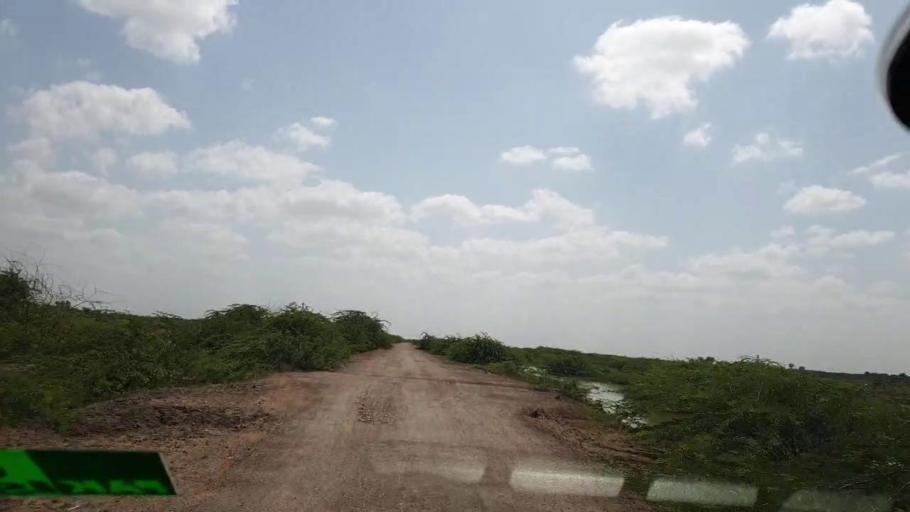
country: PK
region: Sindh
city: Kadhan
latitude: 24.5959
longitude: 69.1832
